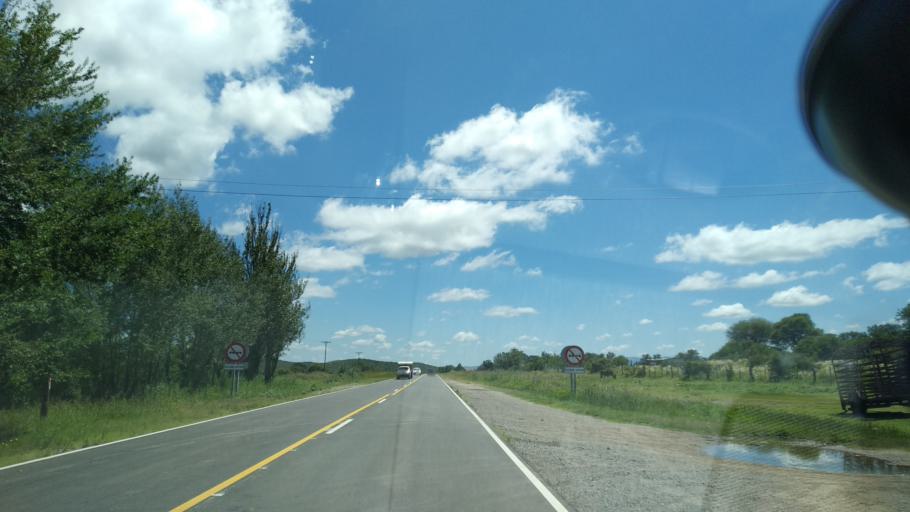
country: AR
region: Cordoba
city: Salsacate
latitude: -31.3620
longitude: -65.1048
